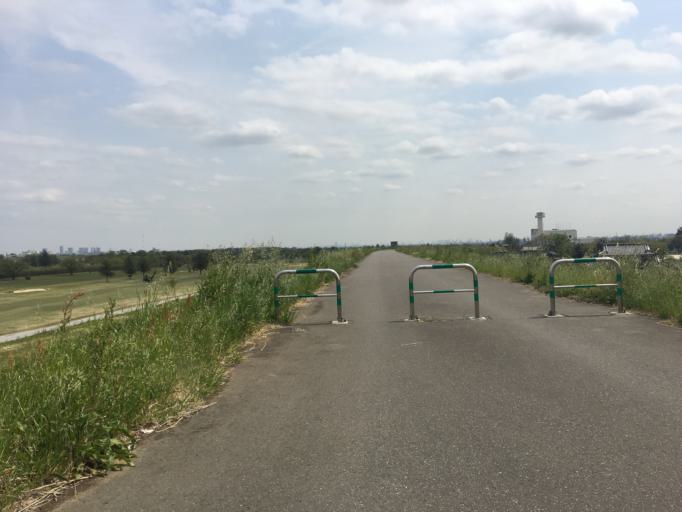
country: JP
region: Saitama
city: Shiki
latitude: 35.8754
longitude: 139.5705
